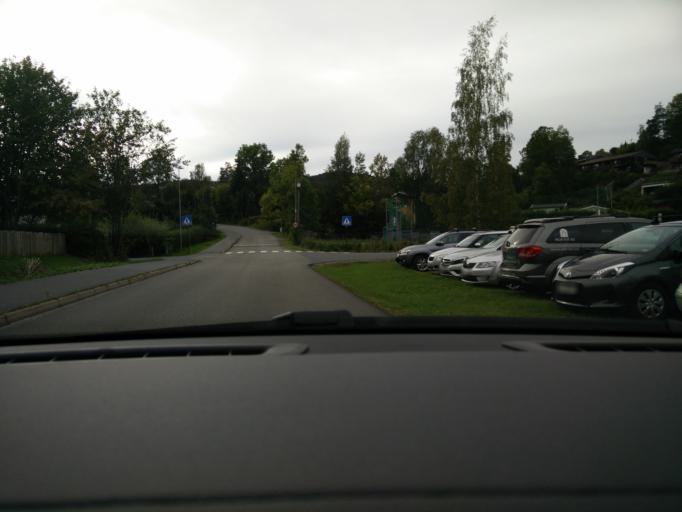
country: NO
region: Akershus
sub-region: Asker
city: Blakstad
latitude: 59.8220
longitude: 10.4488
